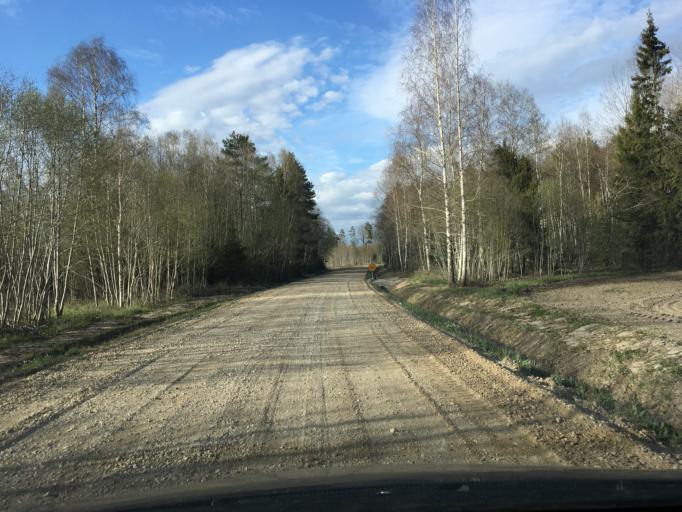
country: EE
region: Raplamaa
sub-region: Maerjamaa vald
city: Marjamaa
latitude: 58.9847
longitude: 24.3630
